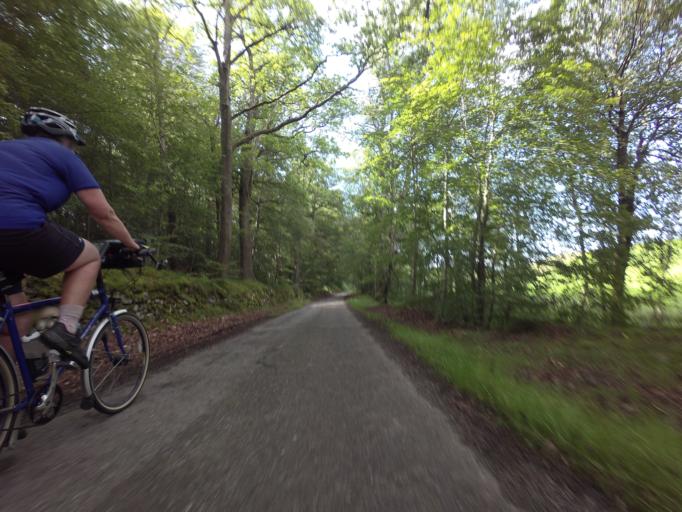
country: GB
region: Scotland
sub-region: Highland
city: Nairn
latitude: 57.5452
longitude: -3.8617
